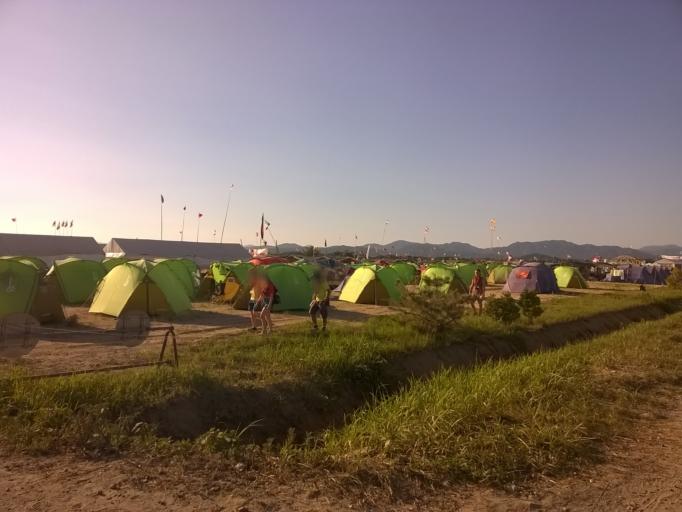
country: JP
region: Yamaguchi
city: Ogori-shimogo
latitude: 34.0196
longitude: 131.3729
